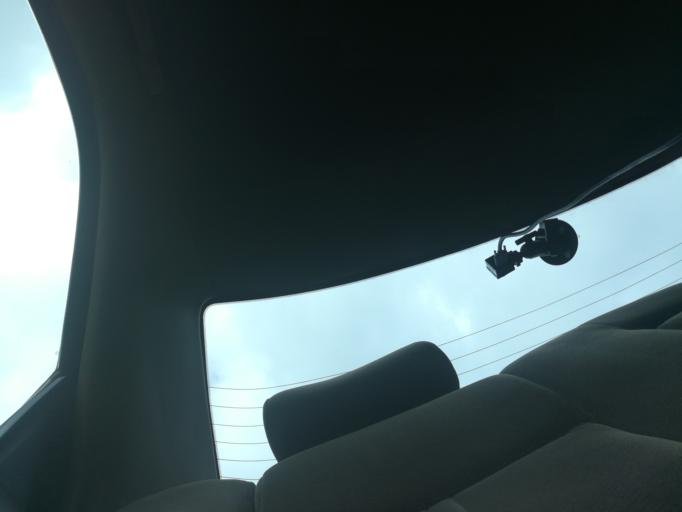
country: NG
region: Lagos
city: Ikorodu
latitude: 6.6531
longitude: 3.5787
